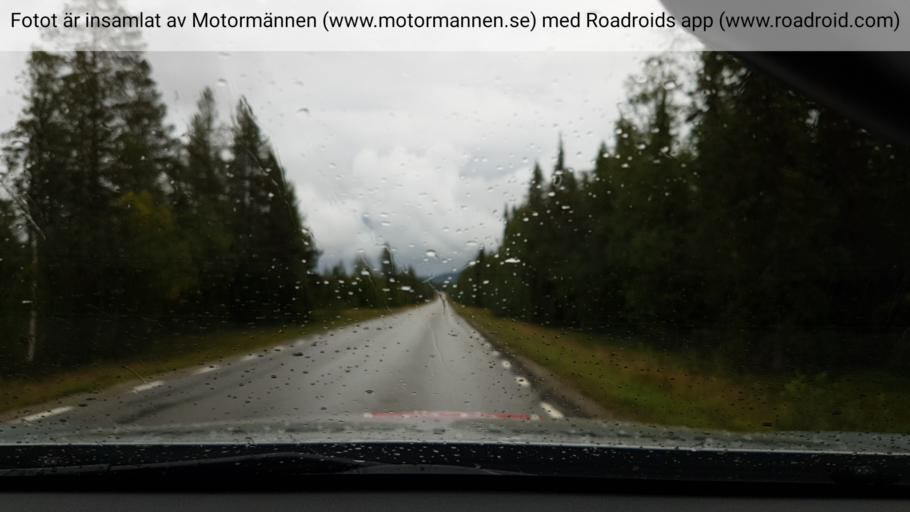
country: SE
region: Vaesterbotten
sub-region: Lycksele Kommun
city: Soderfors
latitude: 64.7055
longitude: 17.7212
